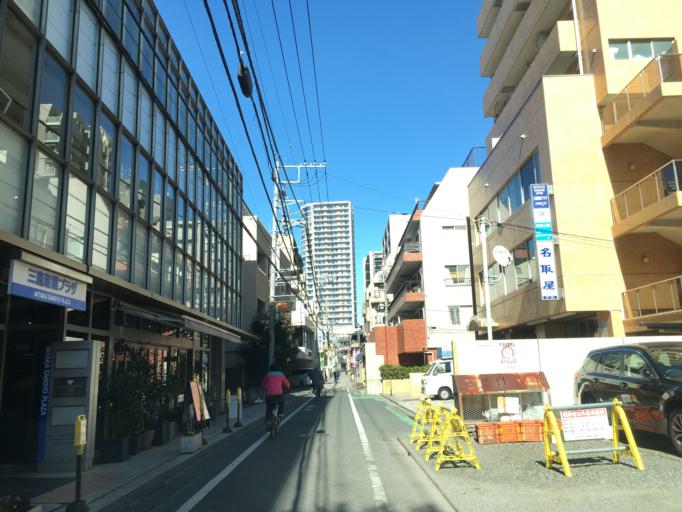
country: JP
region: Tokyo
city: Kamirenjaku
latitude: 35.6987
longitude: 139.5604
